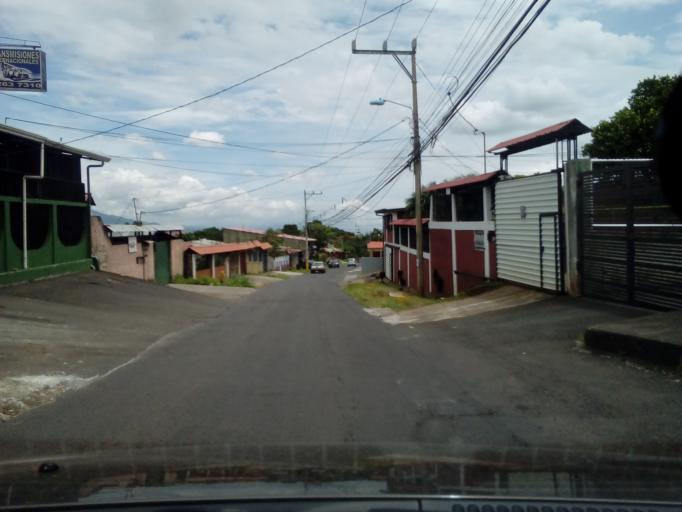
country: CR
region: Heredia
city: San Rafael
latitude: 10.0151
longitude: -84.1117
